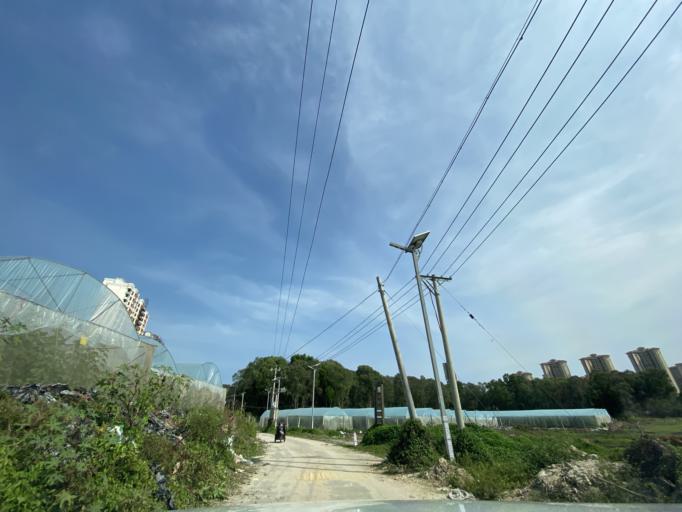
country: CN
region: Hainan
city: Yingzhou
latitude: 18.4048
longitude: 109.8381
